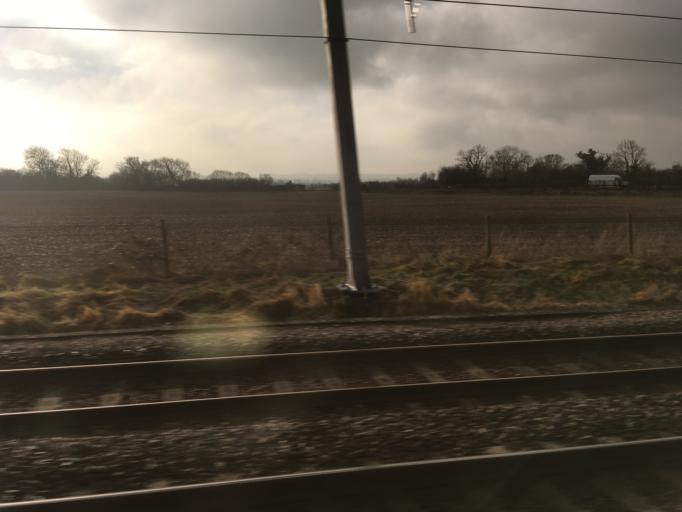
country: GB
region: England
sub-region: Oxfordshire
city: Stanford in the Vale
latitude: 51.6128
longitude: -1.4871
